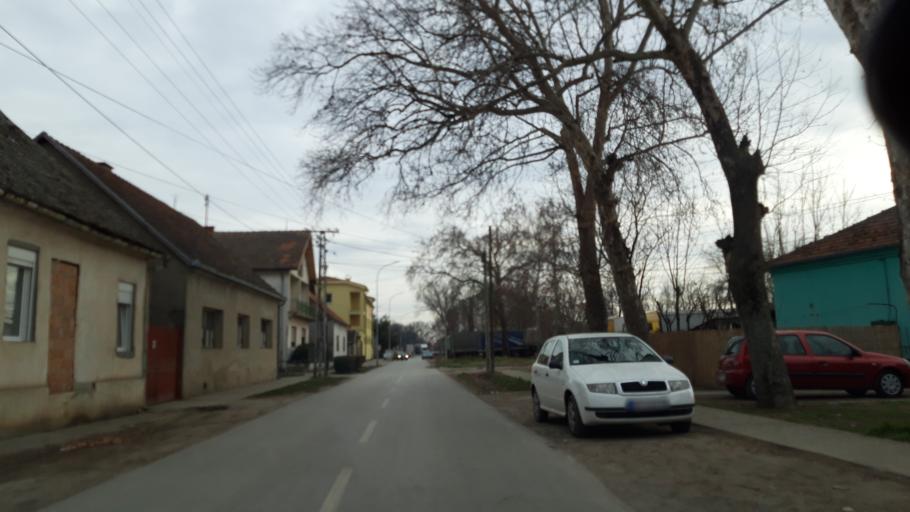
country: RS
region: Autonomna Pokrajina Vojvodina
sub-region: Sremski Okrug
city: Ingija
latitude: 45.0529
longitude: 20.0867
